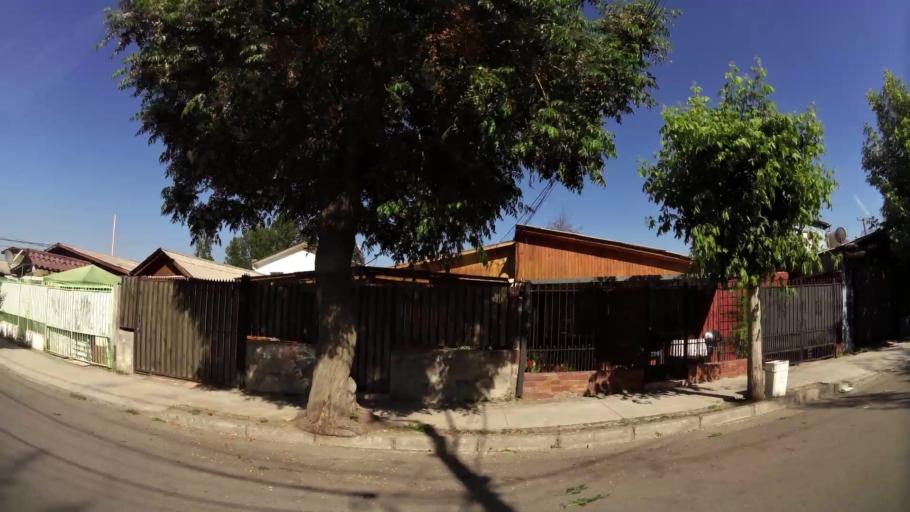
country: CL
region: Santiago Metropolitan
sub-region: Provincia de Maipo
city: San Bernardo
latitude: -33.5682
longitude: -70.6978
